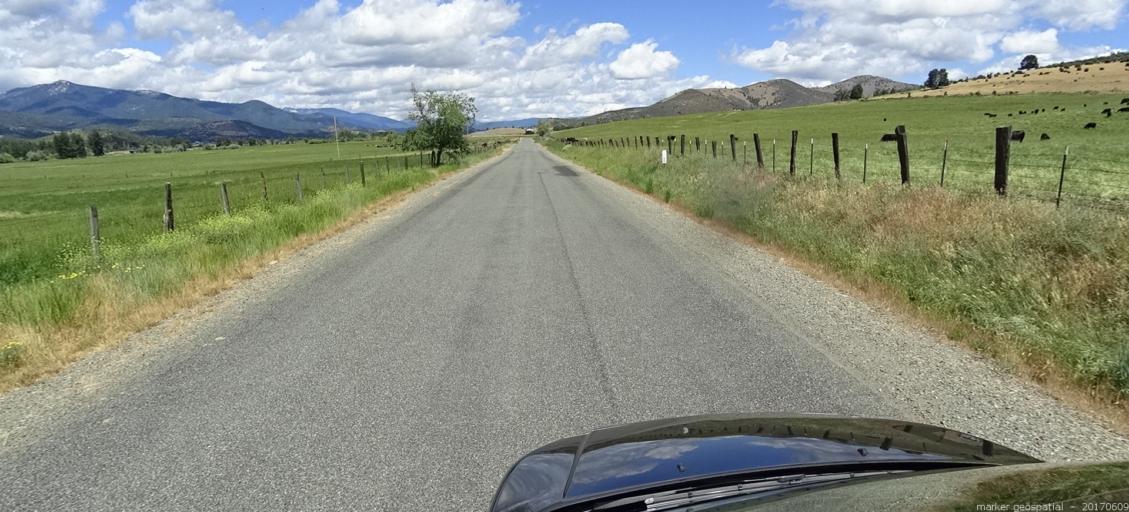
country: US
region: California
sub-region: Siskiyou County
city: Yreka
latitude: 41.3907
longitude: -122.8230
